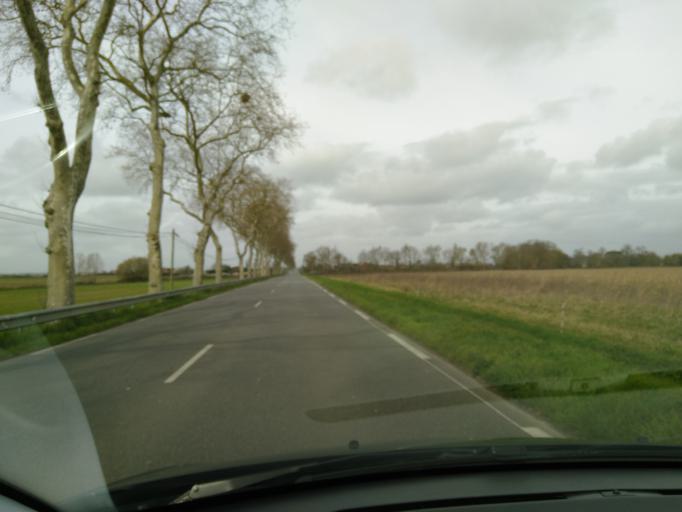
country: FR
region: Midi-Pyrenees
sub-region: Departement de la Haute-Garonne
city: Merville
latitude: 43.7285
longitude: 1.3225
